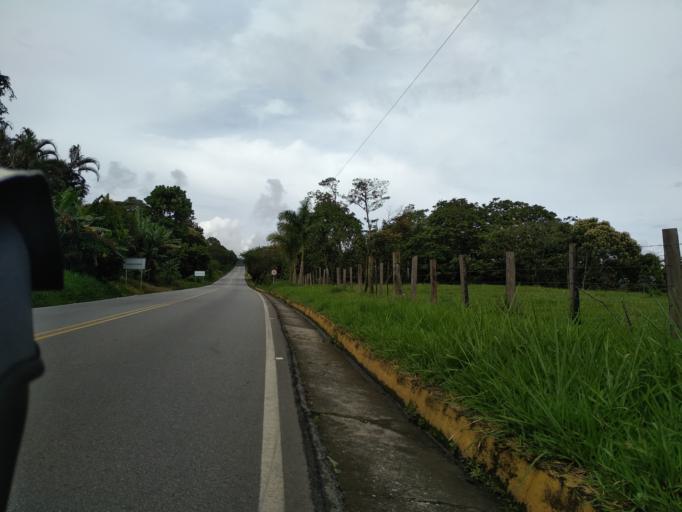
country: CO
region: Santander
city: Suaita
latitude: 6.0943
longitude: -73.3838
